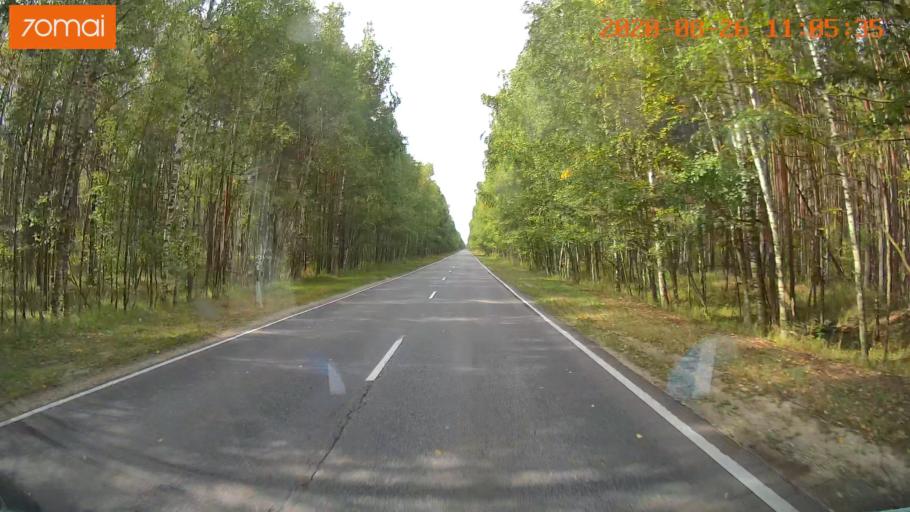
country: RU
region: Rjazan
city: Izhevskoye
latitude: 54.5271
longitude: 41.1686
